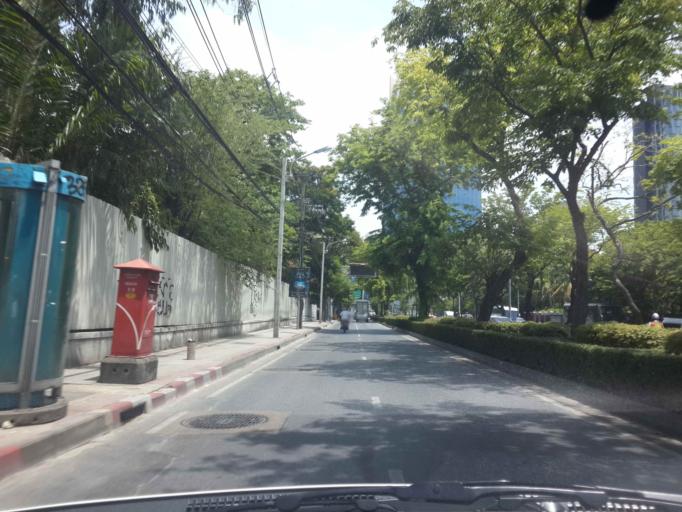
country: TH
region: Bangkok
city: Bang Rak
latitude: 13.7288
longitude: 100.5452
